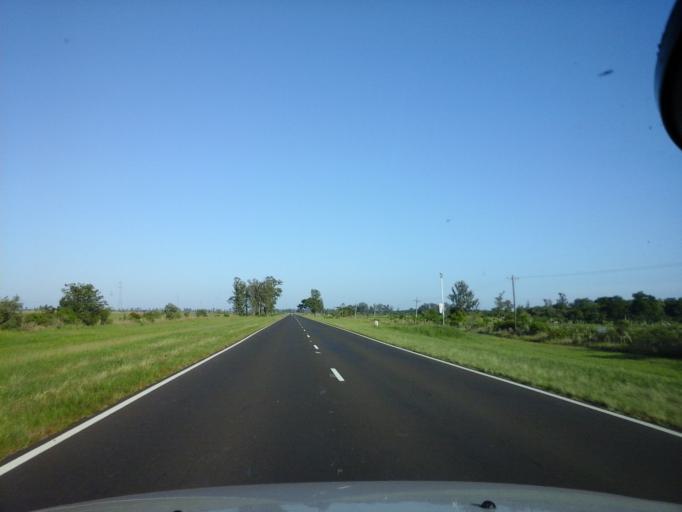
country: AR
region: Corrientes
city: Ita Ibate
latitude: -27.4813
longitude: -57.2916
